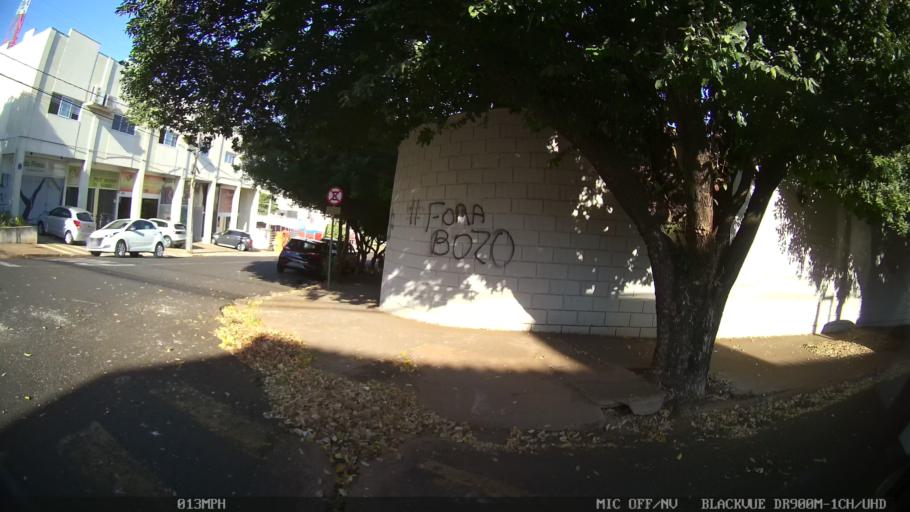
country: BR
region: Sao Paulo
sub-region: Sao Jose Do Rio Preto
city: Sao Jose do Rio Preto
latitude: -20.8216
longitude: -49.4011
